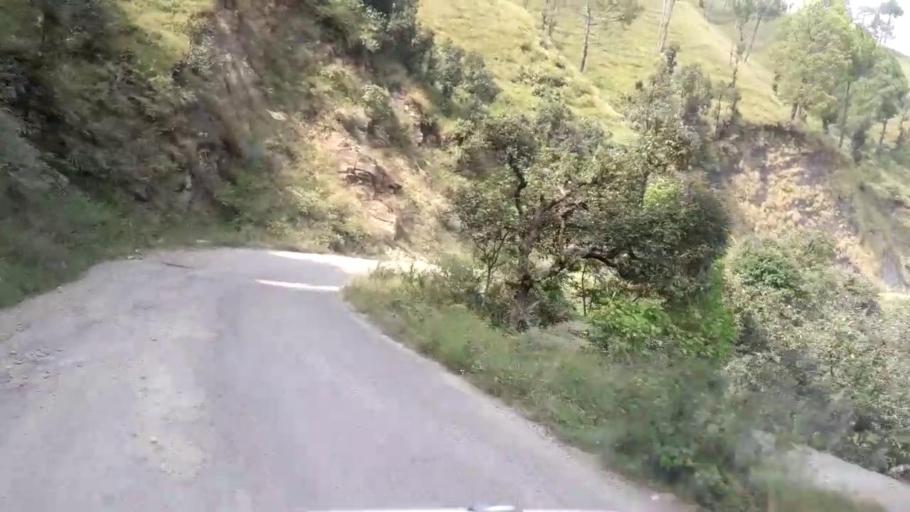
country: IN
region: Himachal Pradesh
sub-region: Shimla
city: Shimla
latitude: 31.0544
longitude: 77.1550
